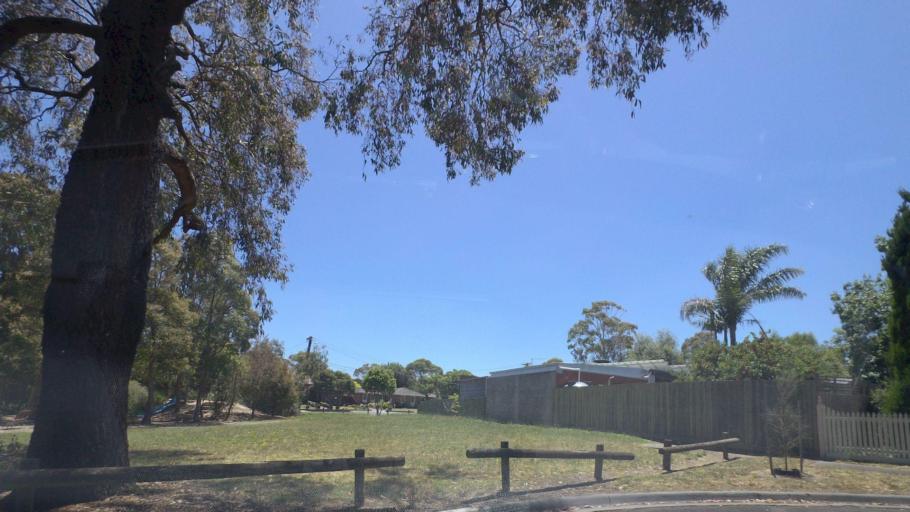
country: AU
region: Victoria
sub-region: Knox
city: Boronia
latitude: -37.8778
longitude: 145.2752
